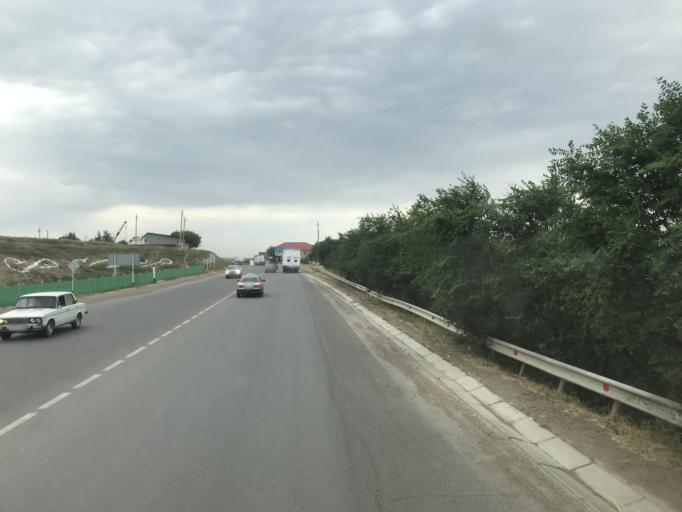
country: KZ
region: Ongtustik Qazaqstan
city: Saryaghash
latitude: 41.4588
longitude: 69.1427
